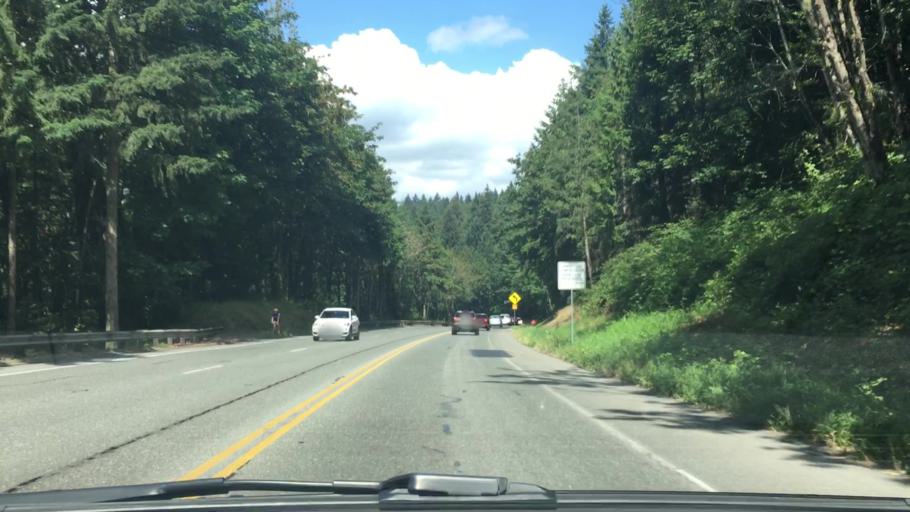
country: US
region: Washington
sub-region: King County
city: City of Sammamish
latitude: 47.5690
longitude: -122.0474
